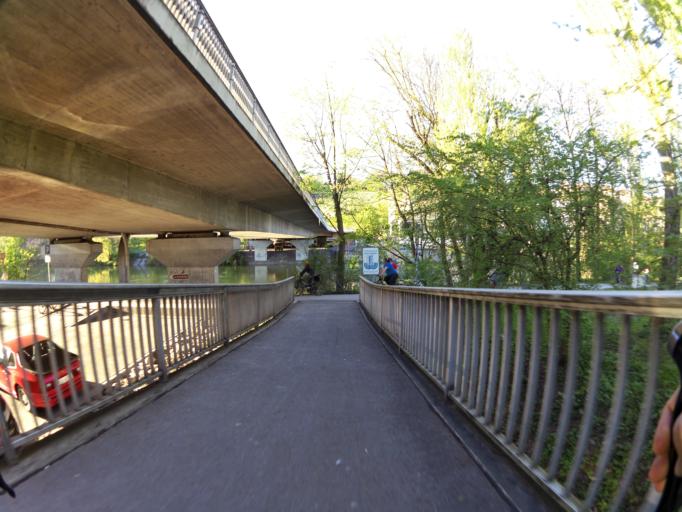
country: CH
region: Zurich
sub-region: Bezirk Zuerich
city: Zuerich (Kreis 10) / Hoengg
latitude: 47.3986
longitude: 8.4951
